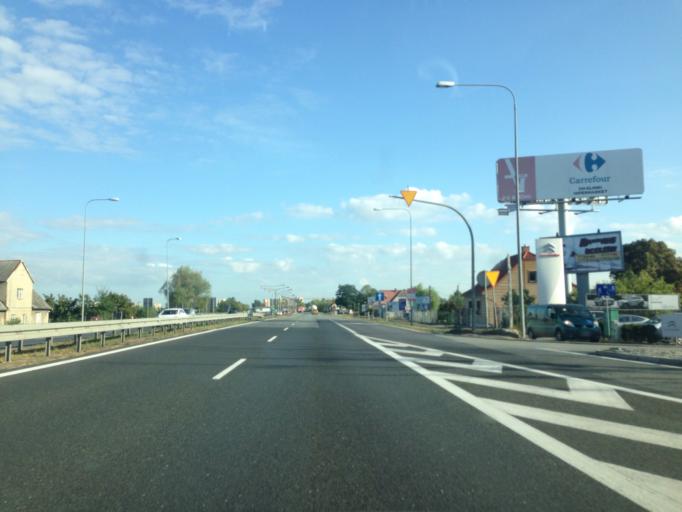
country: PL
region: Kujawsko-Pomorskie
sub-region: Bydgoszcz
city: Bydgoszcz
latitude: 53.0952
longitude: 18.0086
